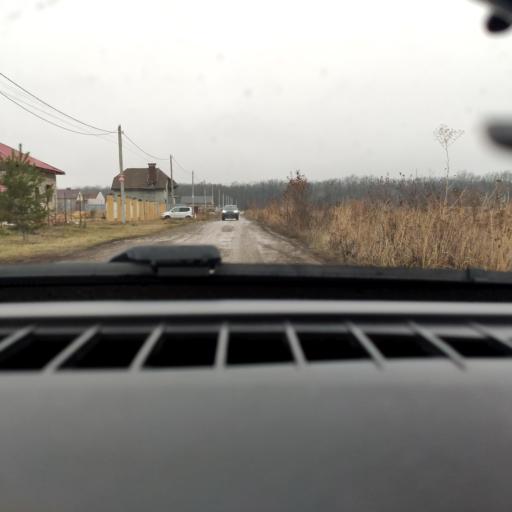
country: RU
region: Voronezj
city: Semiluki
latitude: 51.6604
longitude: 39.0430
